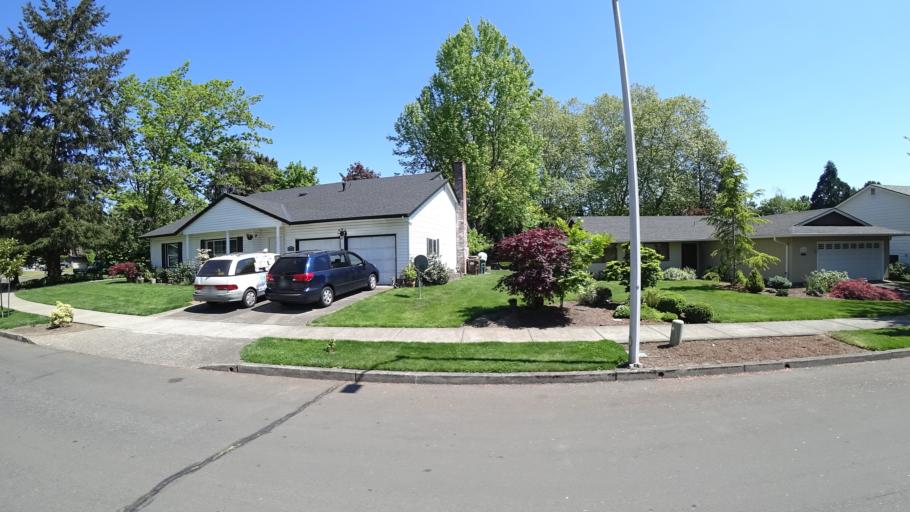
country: US
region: Oregon
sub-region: Washington County
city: Hillsboro
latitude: 45.5019
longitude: -122.9610
